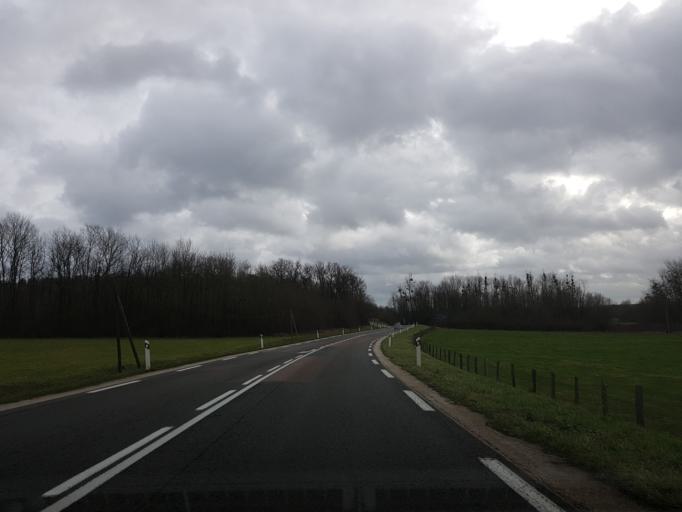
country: FR
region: Champagne-Ardenne
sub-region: Departement de la Haute-Marne
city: Chalindrey
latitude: 47.8229
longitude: 5.4815
